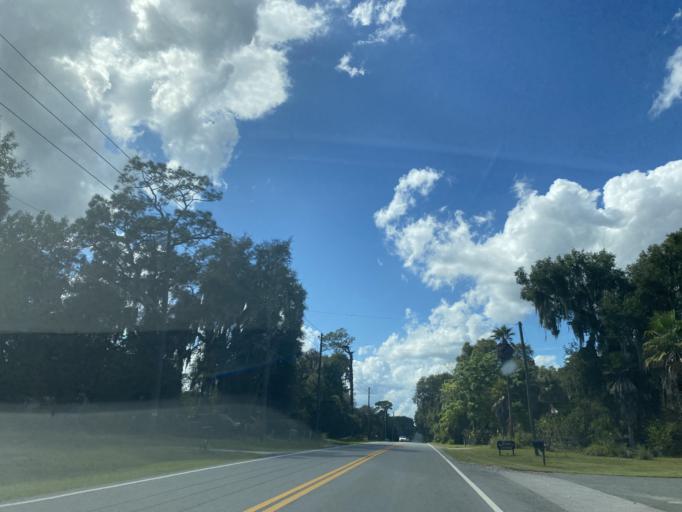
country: US
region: Florida
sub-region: Sumter County
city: The Villages
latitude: 28.9820
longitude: -81.9701
